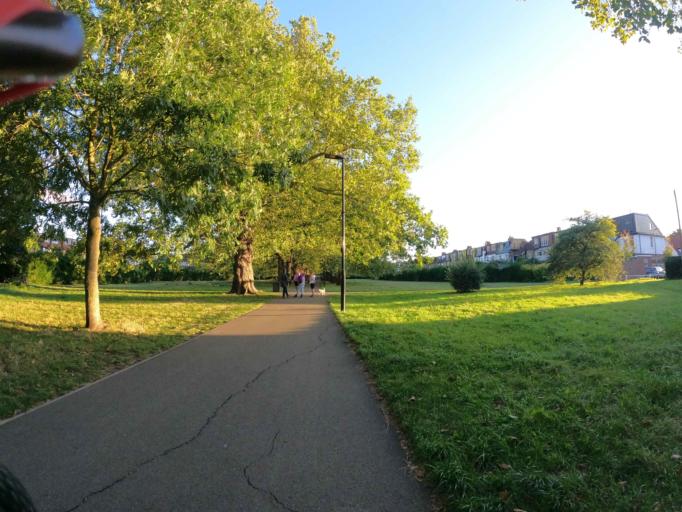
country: GB
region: England
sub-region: Greater London
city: Ealing Broadway
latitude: 51.5278
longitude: -0.3194
